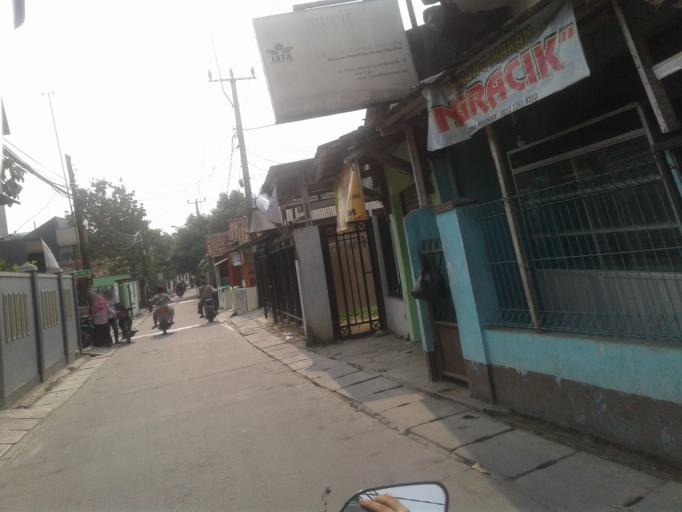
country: ID
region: West Java
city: Depok
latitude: -6.3729
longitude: 106.8378
